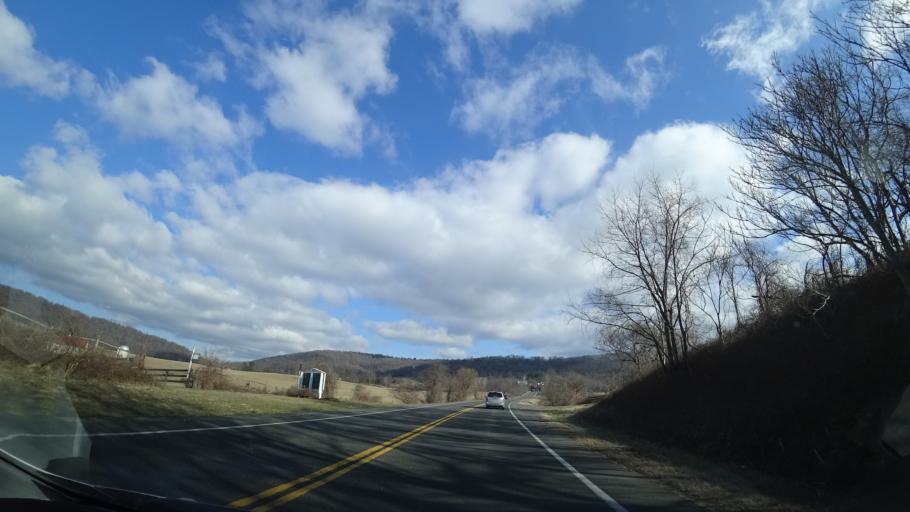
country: US
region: Virginia
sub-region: Warren County
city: Shenandoah Farms
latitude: 38.9976
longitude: -77.9487
